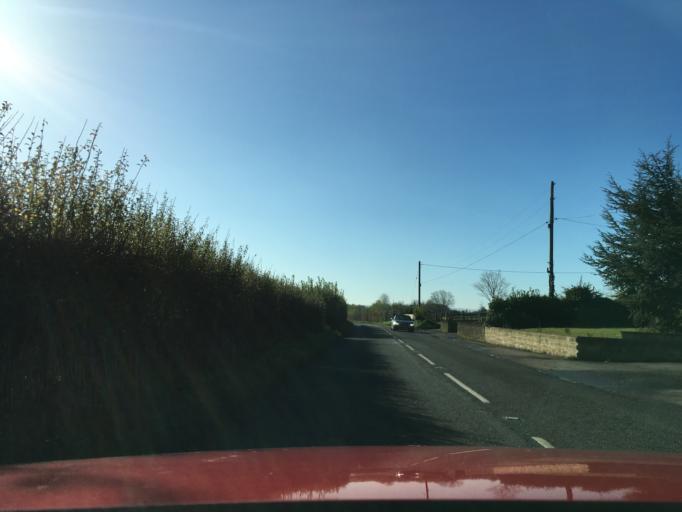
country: GB
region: England
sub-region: Somerset
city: Martock
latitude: 51.0004
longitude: -2.7654
